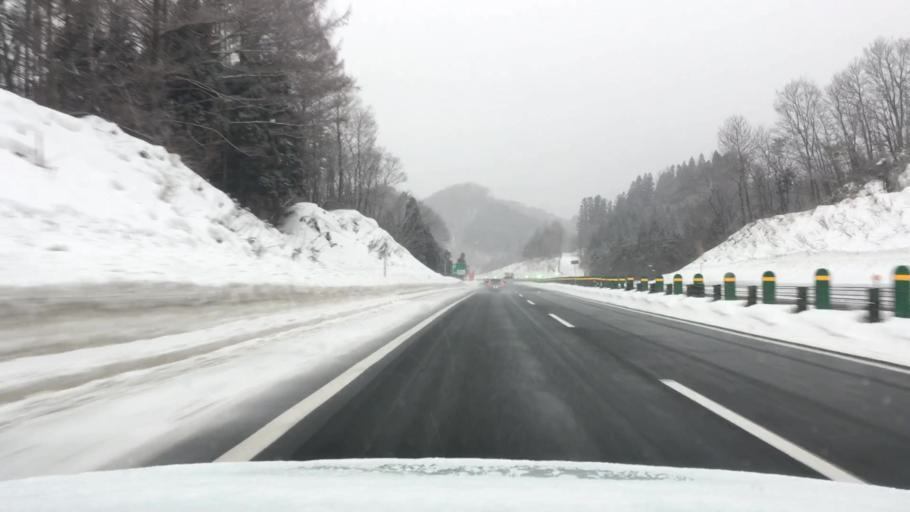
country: JP
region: Akita
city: Hanawa
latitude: 40.1346
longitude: 140.9751
